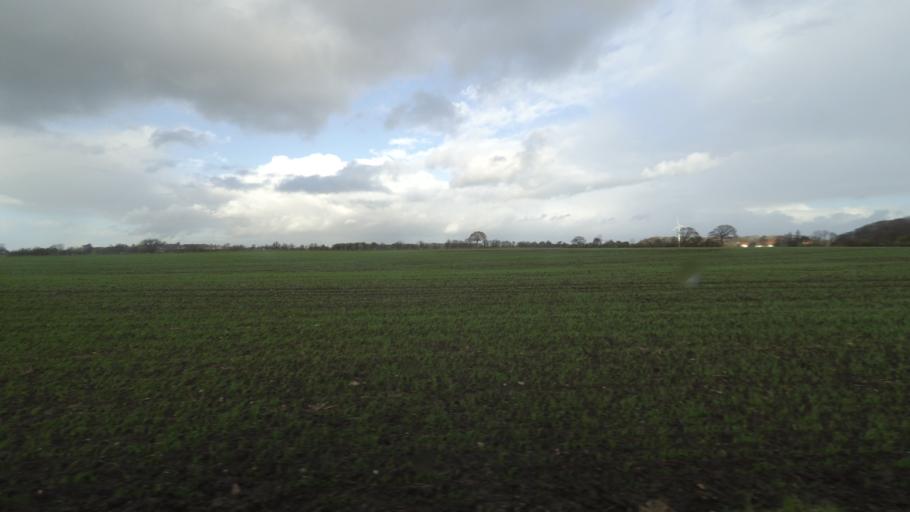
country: DK
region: Central Jutland
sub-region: Odder Kommune
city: Odder
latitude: 55.9009
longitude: 10.1936
